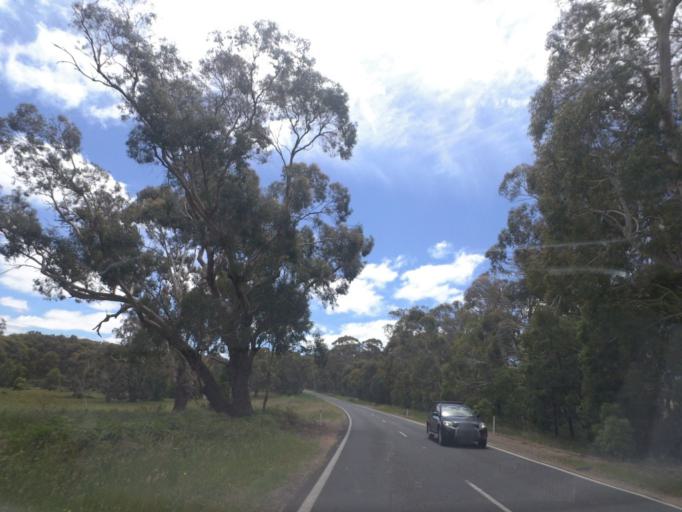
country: AU
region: Victoria
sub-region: Mount Alexander
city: Castlemaine
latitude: -37.3309
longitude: 144.1667
